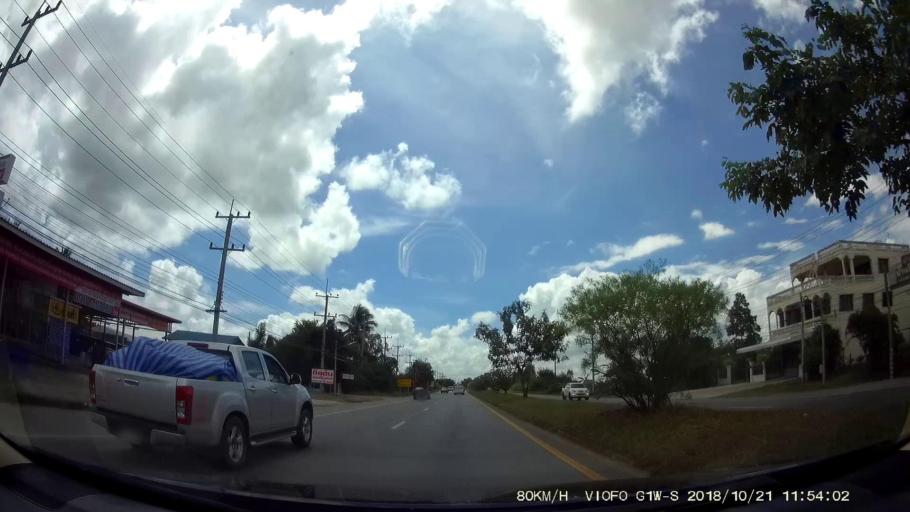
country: TH
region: Chaiyaphum
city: Chatturat
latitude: 15.5891
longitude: 101.9032
